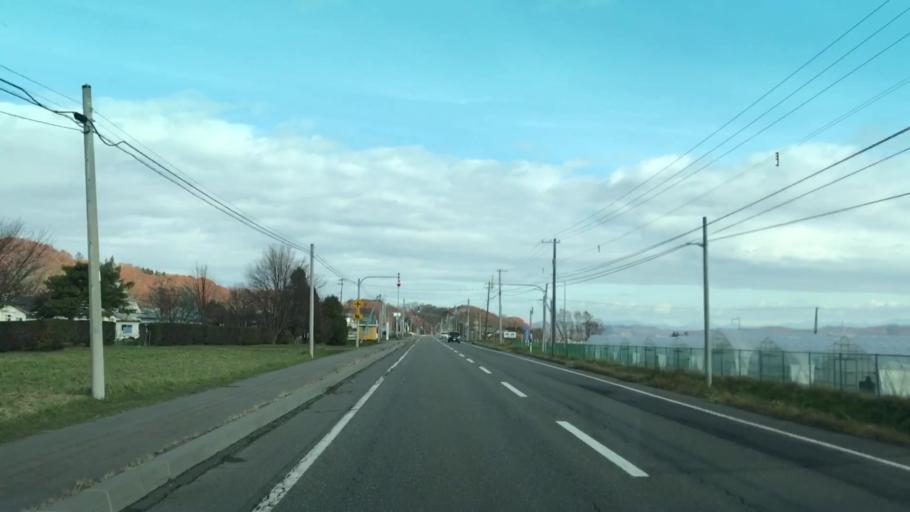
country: JP
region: Hokkaido
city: Shizunai-furukawacho
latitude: 42.5547
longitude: 142.0760
